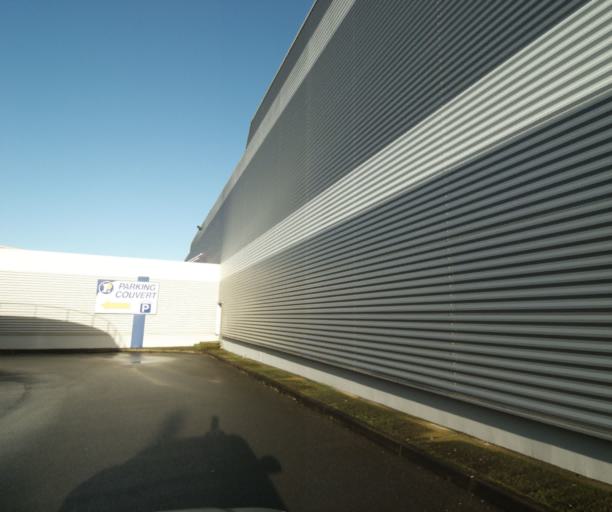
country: FR
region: Pays de la Loire
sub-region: Departement de la Sarthe
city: Sarge-les-le-Mans
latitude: 48.0224
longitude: 0.2246
